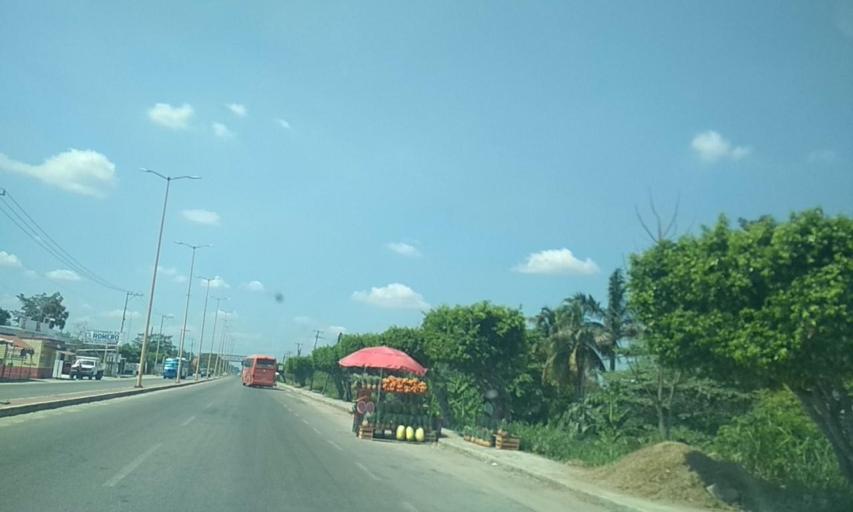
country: MX
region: Tabasco
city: Huimanguillo
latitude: 17.8388
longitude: -93.3977
